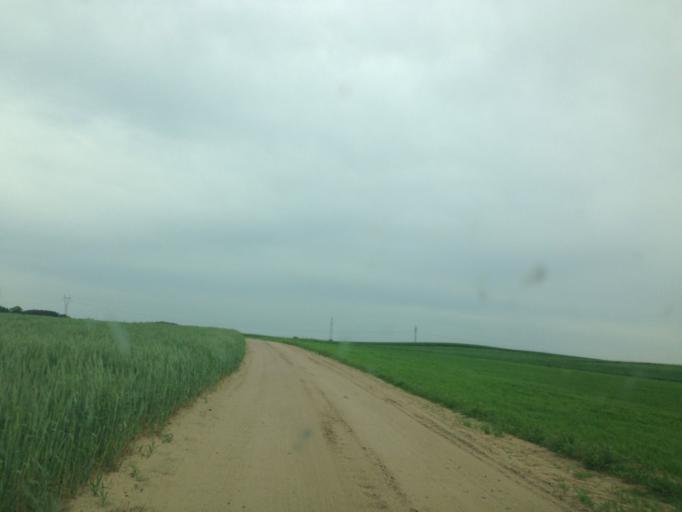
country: PL
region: Kujawsko-Pomorskie
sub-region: Powiat brodnicki
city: Bartniczka
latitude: 53.2681
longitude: 19.6134
